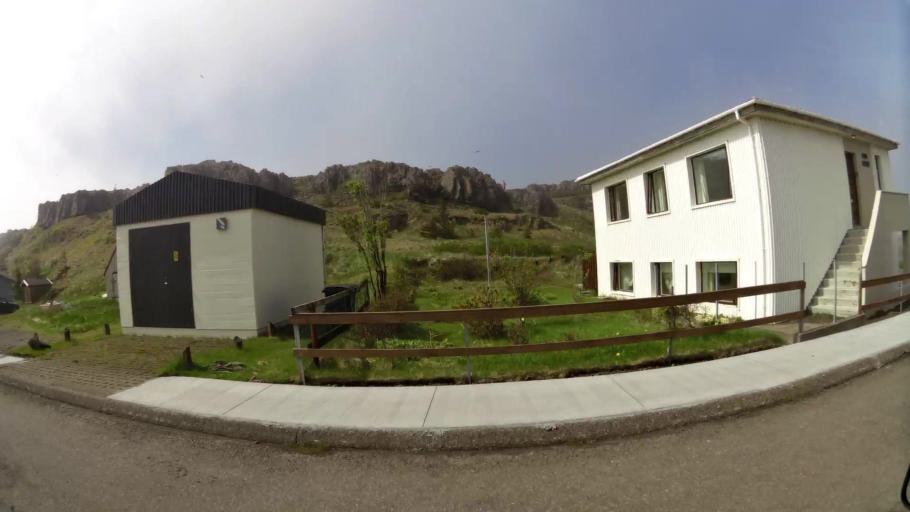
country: IS
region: East
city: Reydarfjoerdur
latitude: 64.6551
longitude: -14.2813
